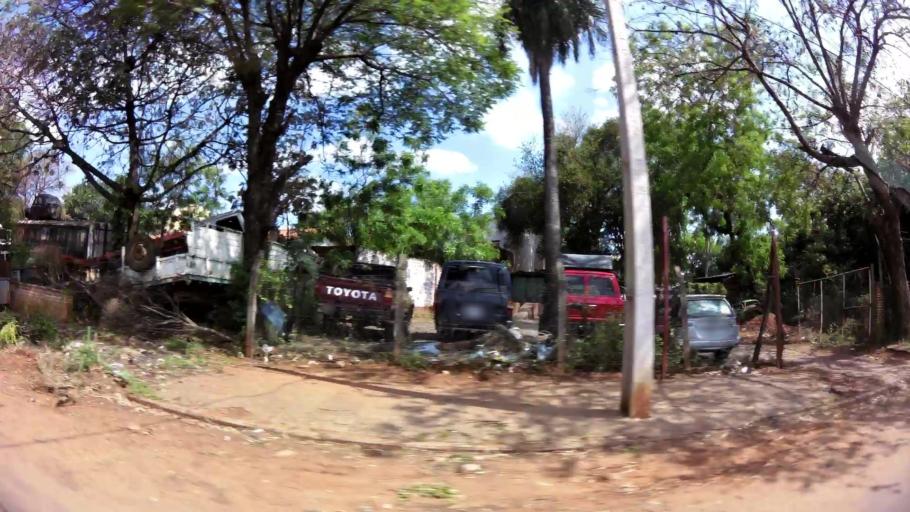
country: PY
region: Central
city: San Lorenzo
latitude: -25.3399
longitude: -57.5013
